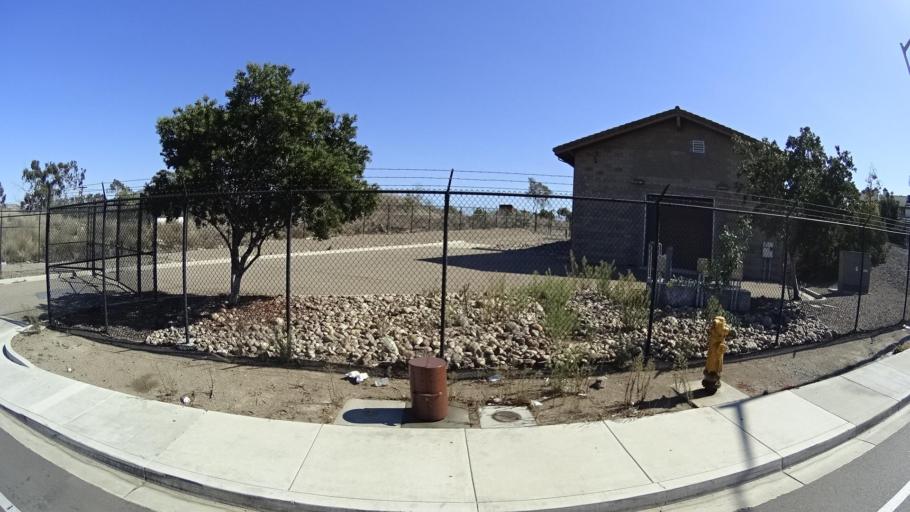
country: US
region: California
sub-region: San Diego County
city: La Presa
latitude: 32.7017
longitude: -117.0134
